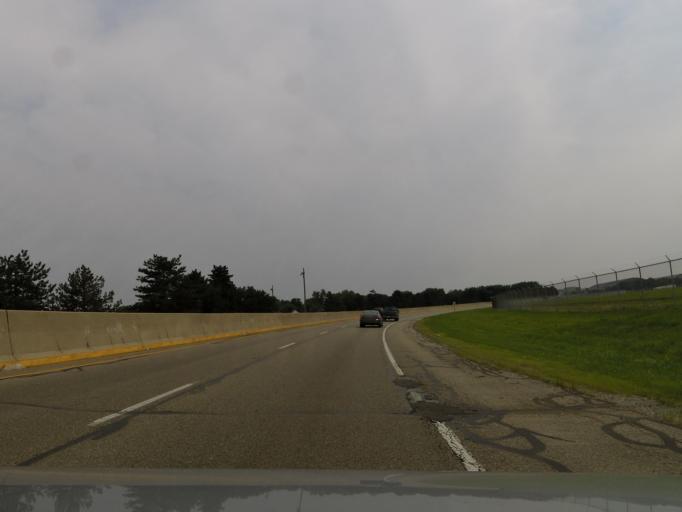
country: US
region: Ohio
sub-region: Montgomery County
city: Riverside
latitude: 39.7761
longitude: -84.1221
